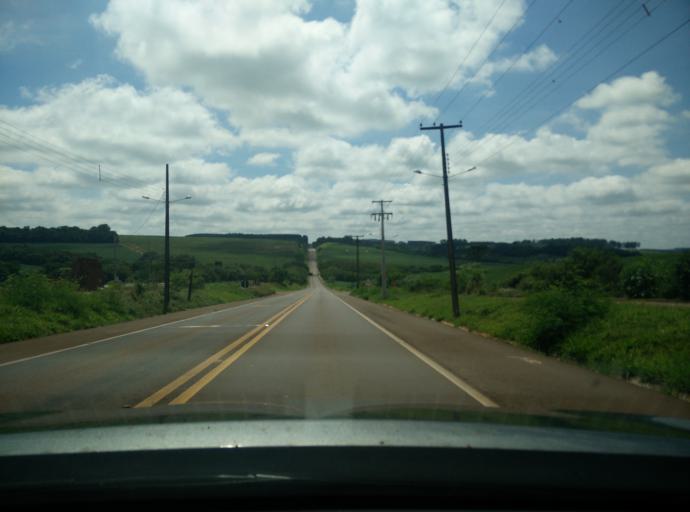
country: BR
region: Parana
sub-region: Campo Mourao
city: Campo Mourao
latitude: -23.9555
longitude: -52.6131
